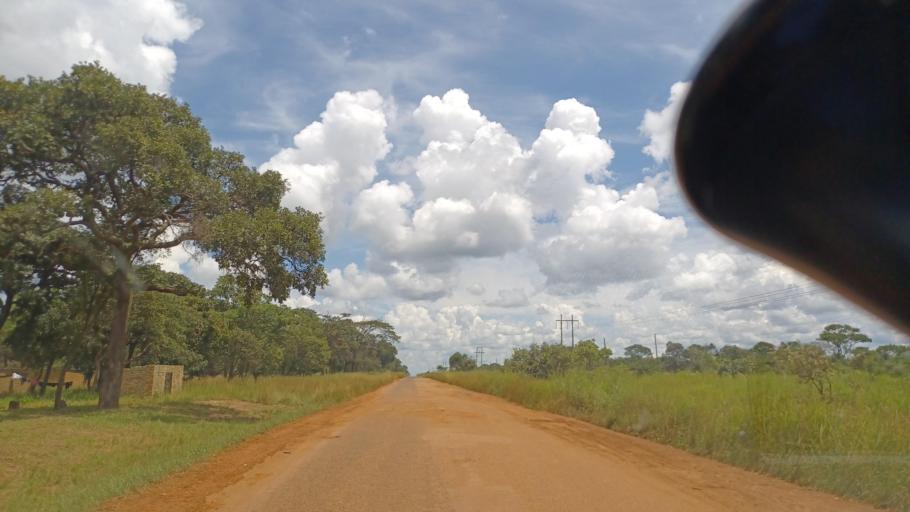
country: ZM
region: North-Western
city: Solwezi
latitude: -12.4916
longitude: 26.1892
